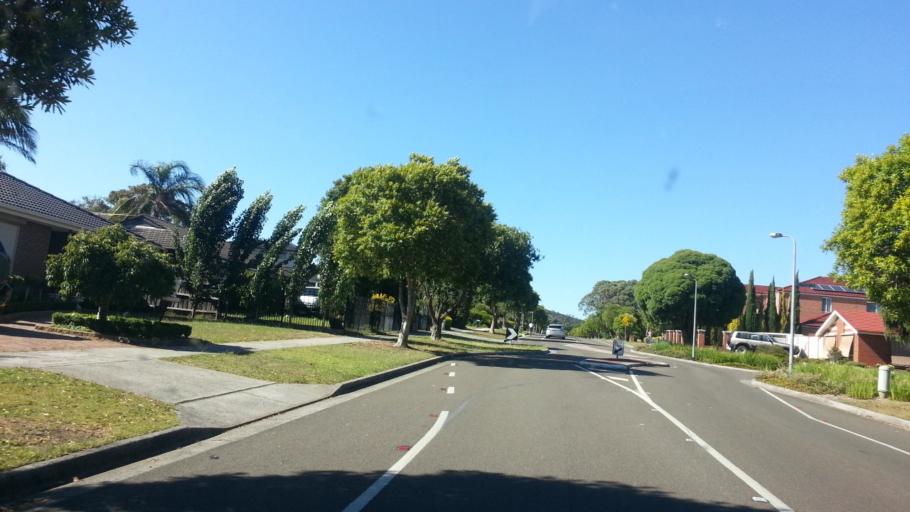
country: AU
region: Victoria
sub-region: Yarra Ranges
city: Lysterfield
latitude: -37.9186
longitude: 145.2693
